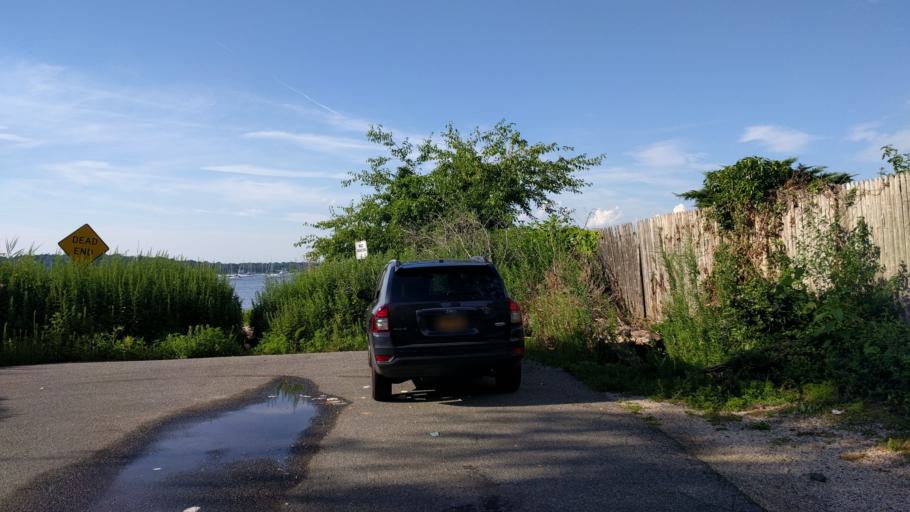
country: US
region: New York
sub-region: Nassau County
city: Oyster Bay Cove
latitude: 40.8733
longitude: -73.5168
